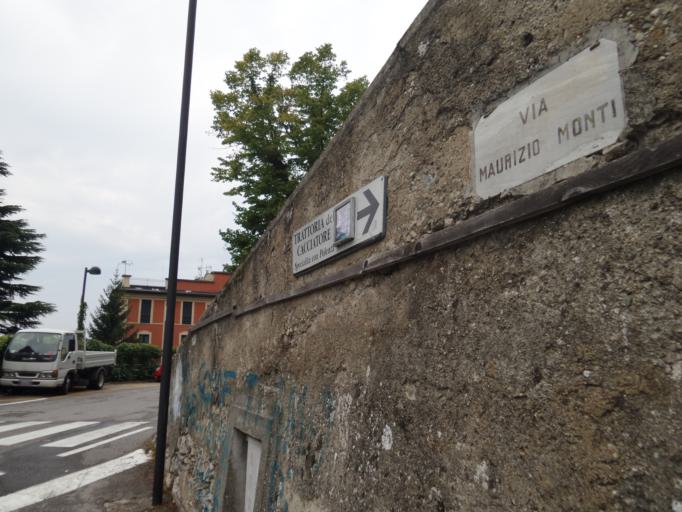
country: IT
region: Lombardy
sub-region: Provincia di Como
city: Brunate
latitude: 45.8181
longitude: 9.0959
